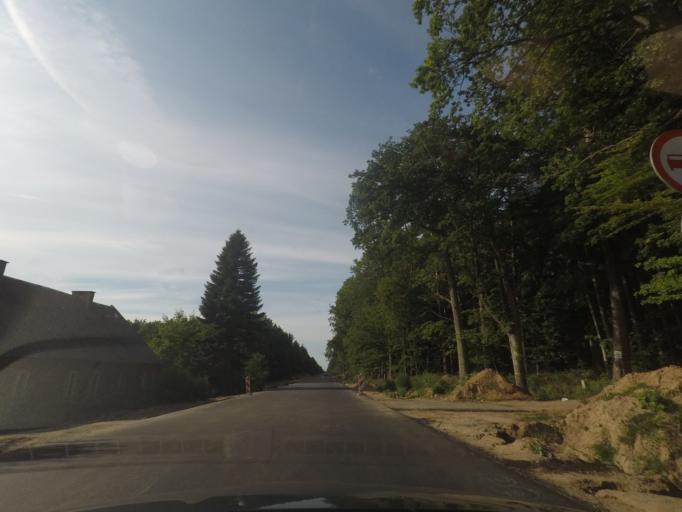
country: PL
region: Pomeranian Voivodeship
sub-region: Powiat leborski
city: Leba
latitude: 54.6958
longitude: 17.5908
